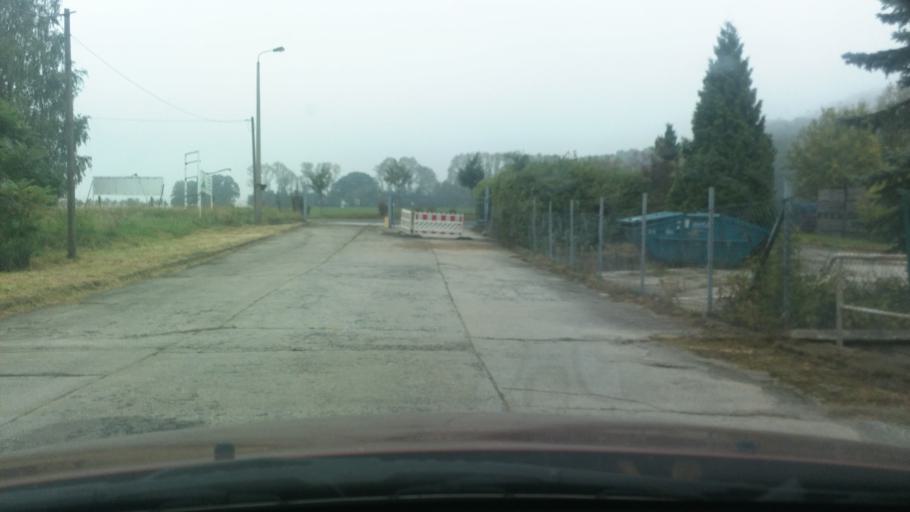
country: DE
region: Saxony
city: Goerlitz
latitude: 51.1237
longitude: 14.9422
